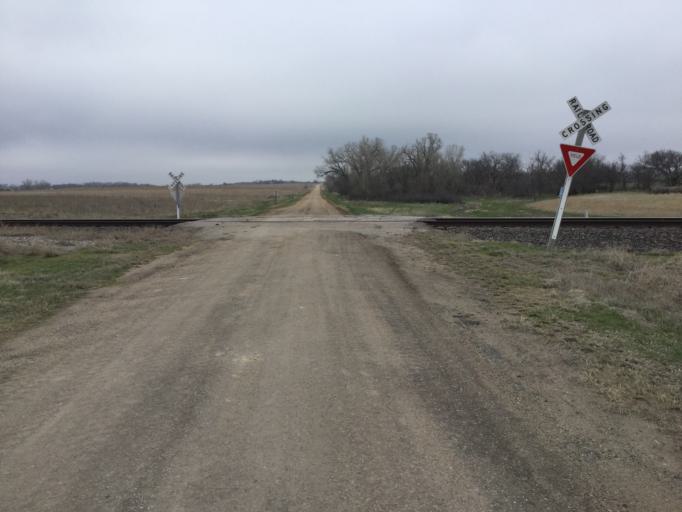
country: US
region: Kansas
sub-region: Ellsworth County
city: Ellsworth
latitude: 38.8333
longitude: -98.5218
